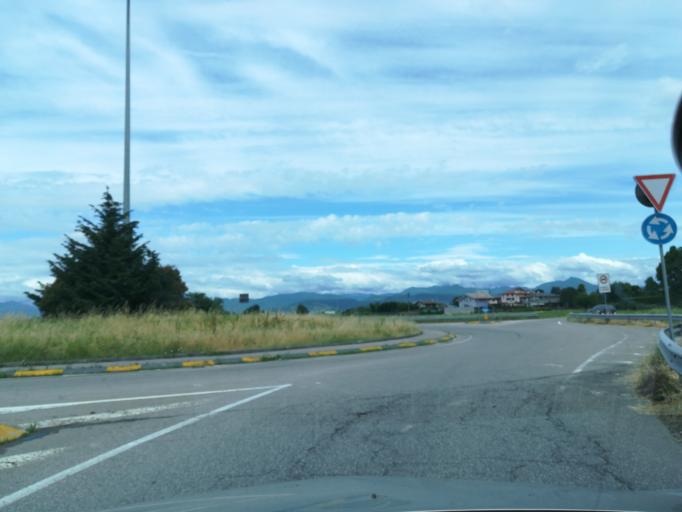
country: IT
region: Lombardy
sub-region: Provincia di Bergamo
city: Cividate al Piano
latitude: 45.5598
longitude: 9.8223
